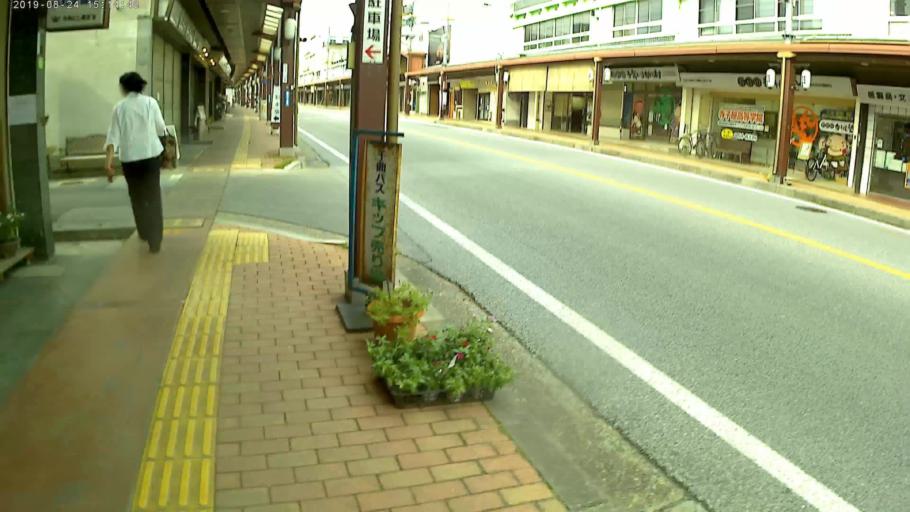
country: JP
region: Nagano
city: Saku
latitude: 36.2728
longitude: 138.4784
